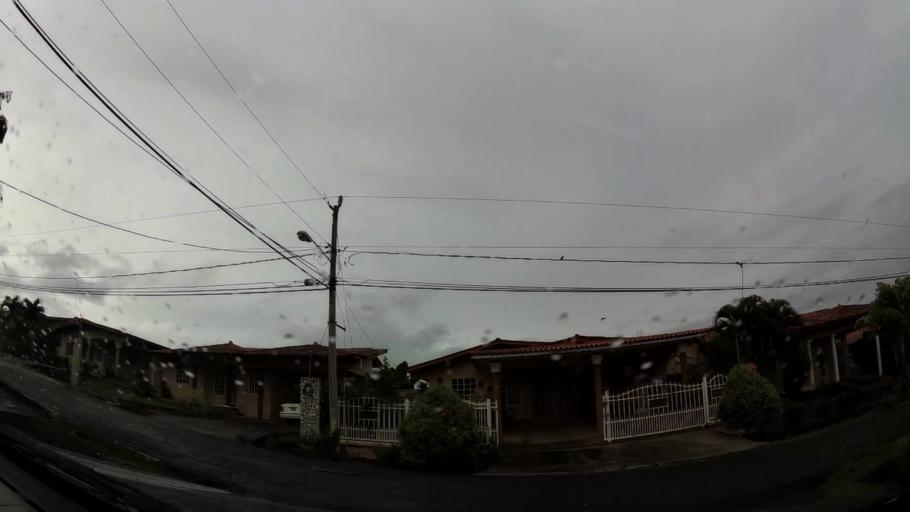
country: PA
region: Veraguas
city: Santiago de Veraguas
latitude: 8.0841
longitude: -80.9863
